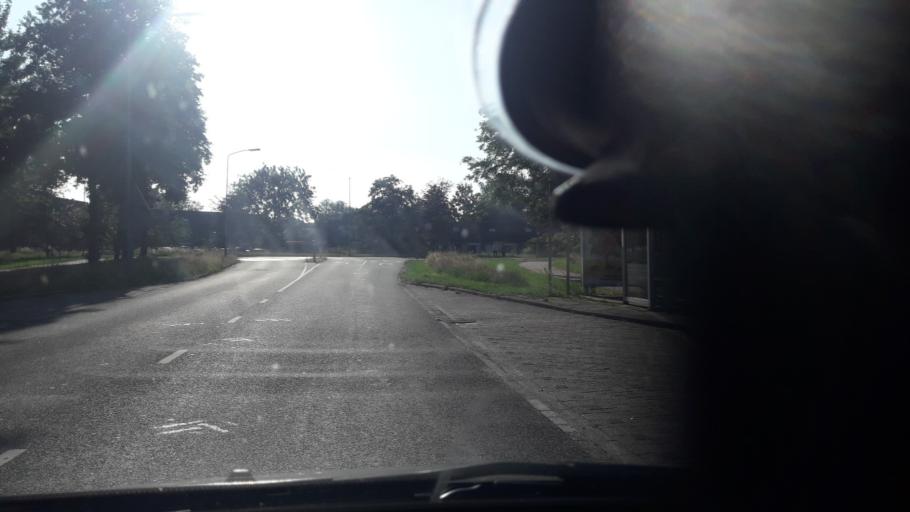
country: NL
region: Gelderland
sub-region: Gemeente Harderwijk
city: Harderwijk
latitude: 52.3387
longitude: 5.6103
